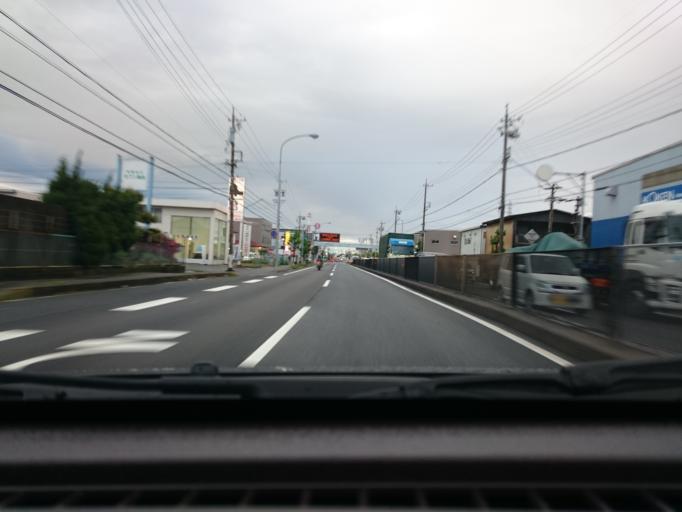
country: JP
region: Mie
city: Yokkaichi
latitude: 34.9724
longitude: 136.6402
